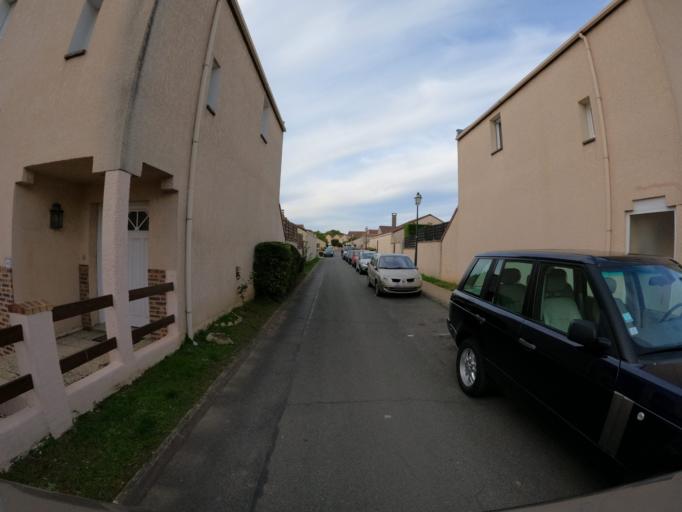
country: FR
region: Ile-de-France
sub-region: Departement de Seine-et-Marne
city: Pontault-Combault
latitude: 48.7925
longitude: 2.6154
